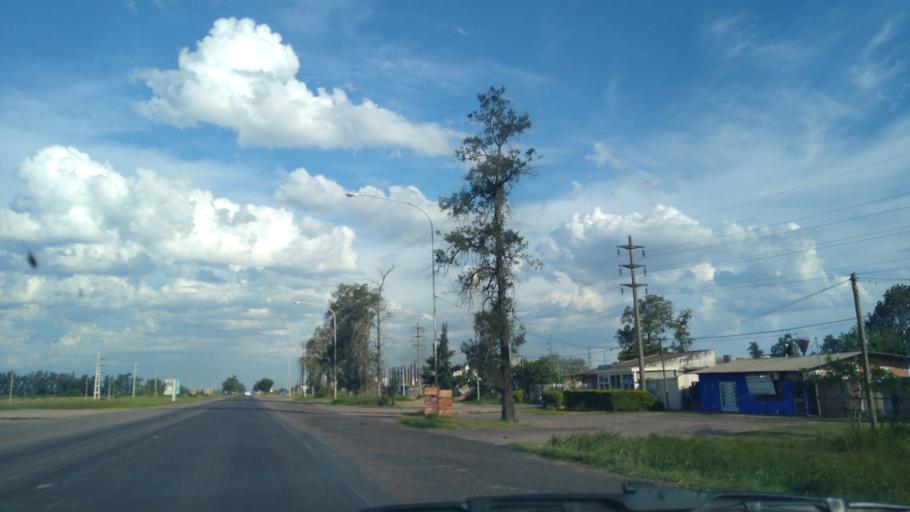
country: AR
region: Chaco
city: Presidencia Roque Saenz Pena
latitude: -26.8139
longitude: -60.4144
